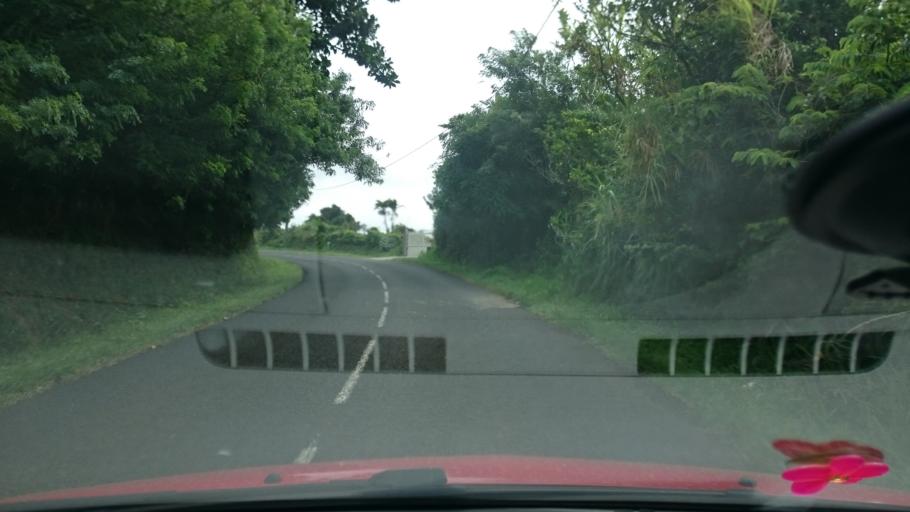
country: MQ
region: Martinique
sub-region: Martinique
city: Riviere-Pilote
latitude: 14.5003
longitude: -60.9239
